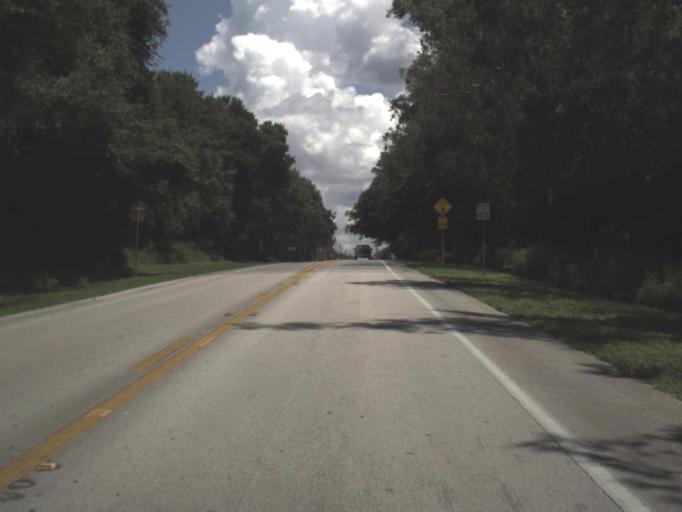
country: US
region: Florida
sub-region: Putnam County
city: Crescent City
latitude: 29.4187
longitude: -81.5100
